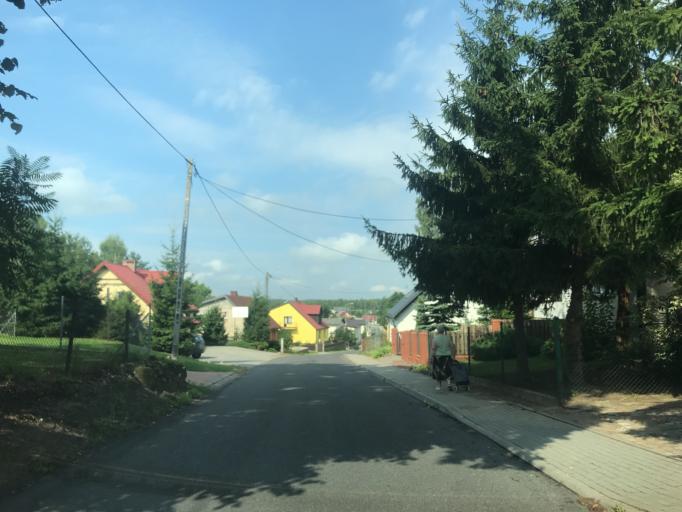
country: PL
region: Warmian-Masurian Voivodeship
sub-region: Powiat nowomiejski
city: Kurzetnik
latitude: 53.3720
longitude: 19.5558
